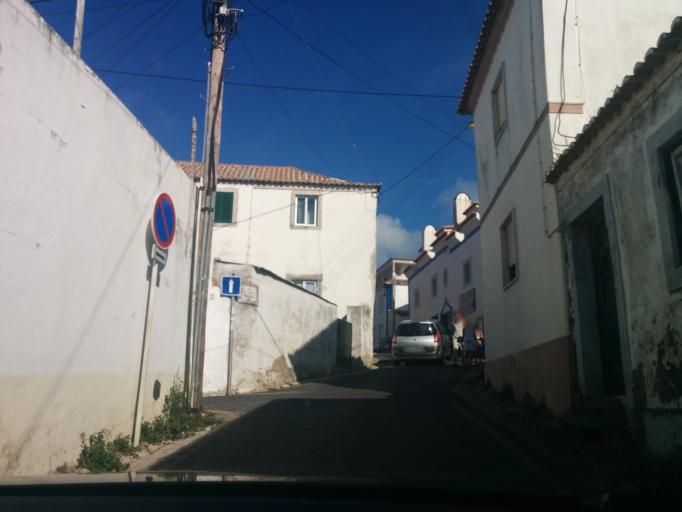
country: PT
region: Lisbon
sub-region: Sintra
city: Colares
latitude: 38.7972
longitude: -9.4722
